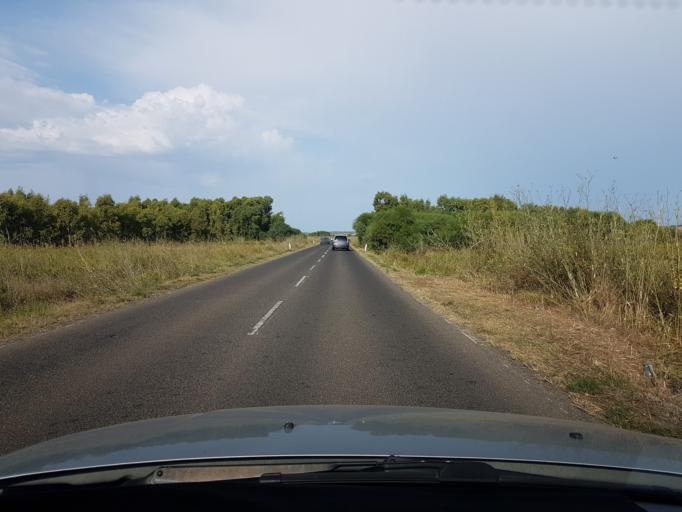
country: IT
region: Sardinia
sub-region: Provincia di Oristano
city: Cabras
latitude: 39.9167
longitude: 8.4858
